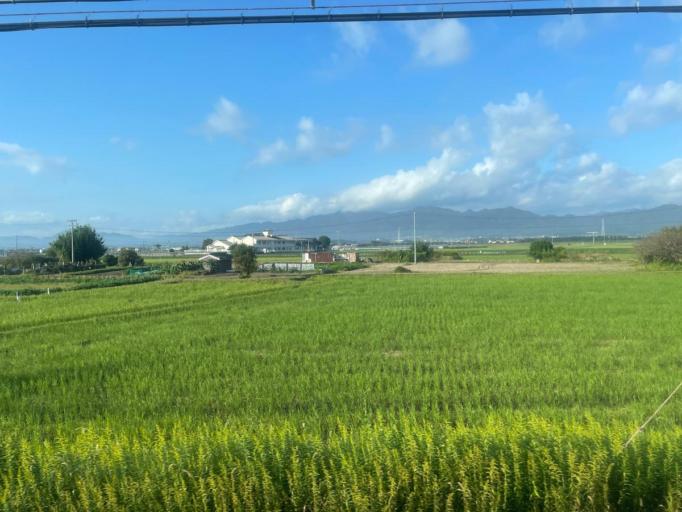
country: JP
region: Mie
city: Hisai-motomachi
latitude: 34.6043
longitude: 136.5111
